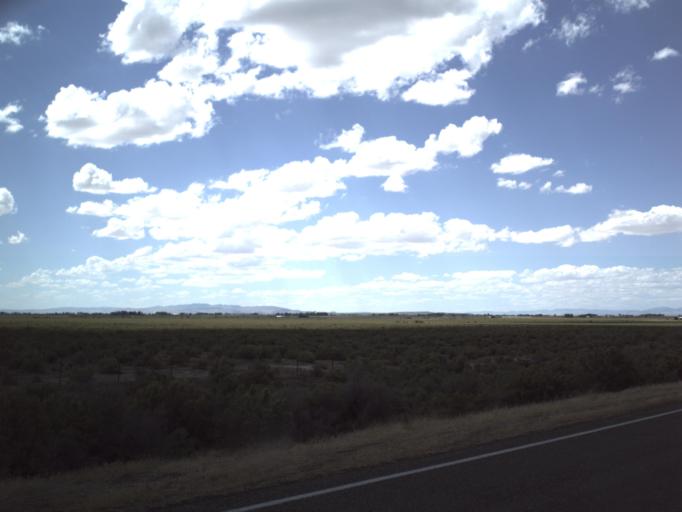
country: US
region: Utah
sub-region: Millard County
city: Delta
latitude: 39.3532
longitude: -112.5084
